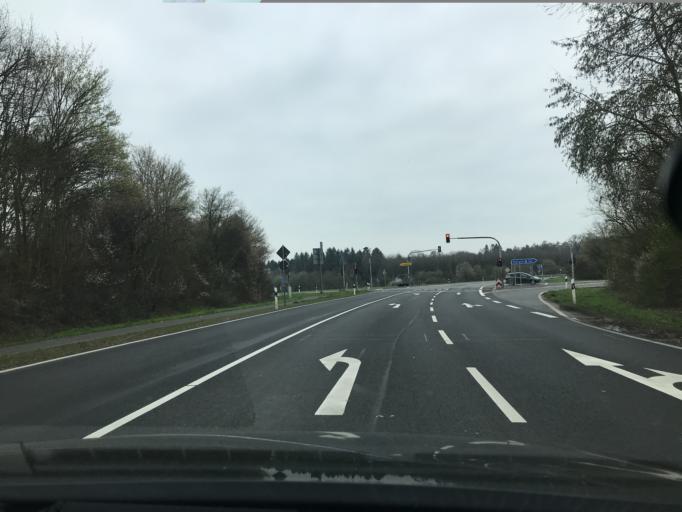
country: DE
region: North Rhine-Westphalia
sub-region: Regierungsbezirk Dusseldorf
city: Schwalmtal
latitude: 51.2072
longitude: 6.2610
